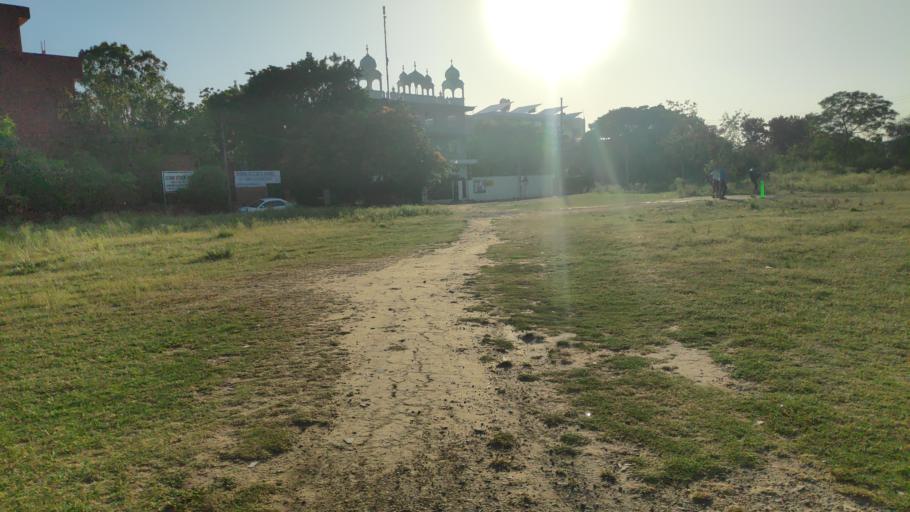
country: IN
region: Chandigarh
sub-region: Chandigarh
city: Chandigarh
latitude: 30.7232
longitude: 76.7520
